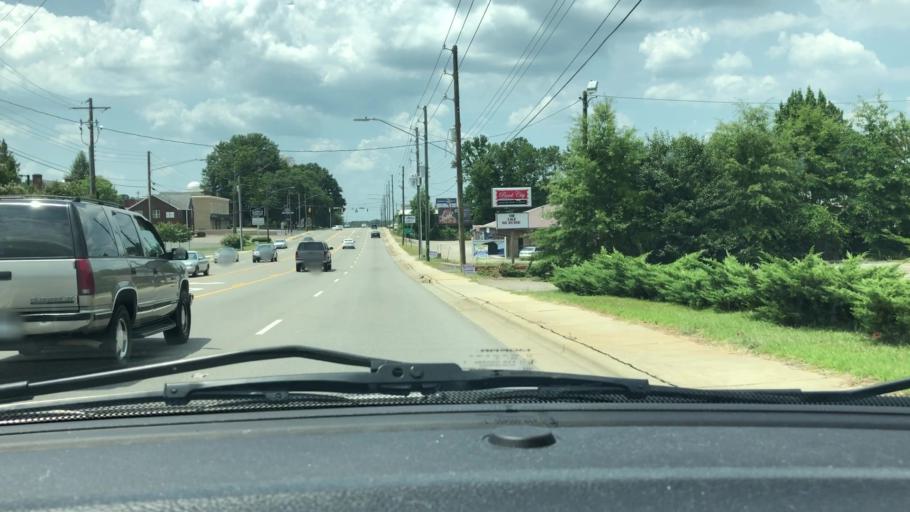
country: US
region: North Carolina
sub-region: Lee County
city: Sanford
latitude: 35.4663
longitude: -79.1600
